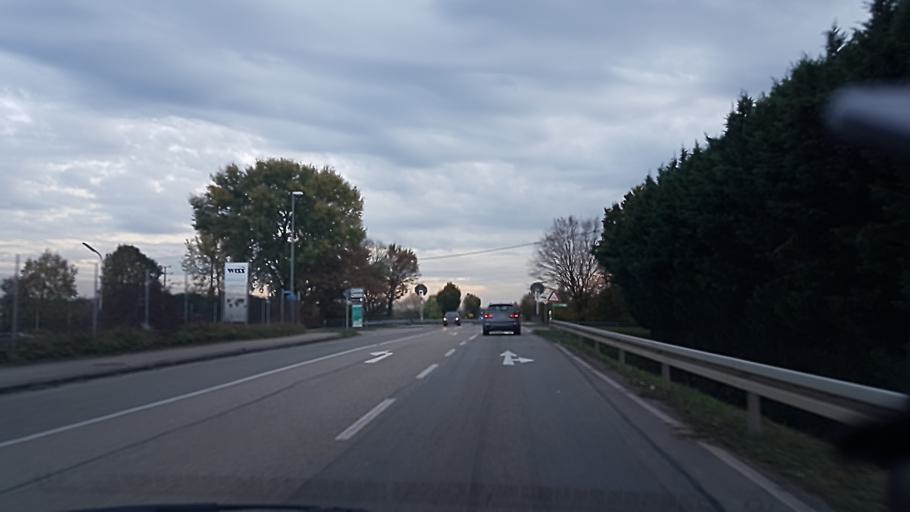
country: DE
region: Baden-Wuerttemberg
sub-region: Freiburg Region
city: Herbolzheim
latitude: 48.2166
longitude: 7.7600
